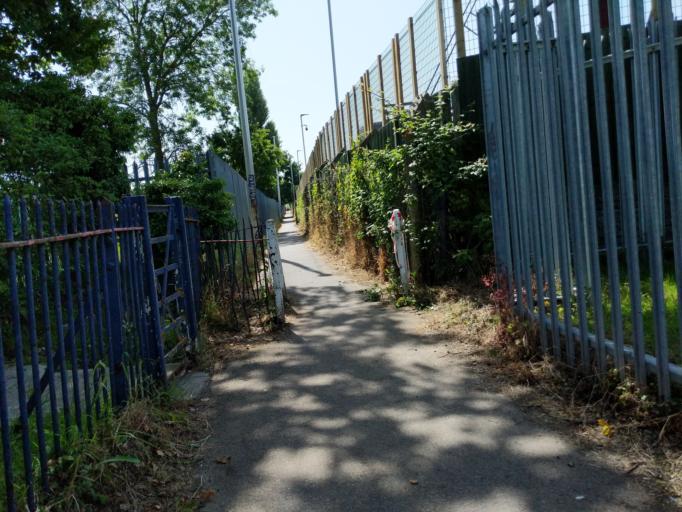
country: GB
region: England
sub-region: Kent
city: Herne Bay
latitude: 51.3641
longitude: 1.1192
